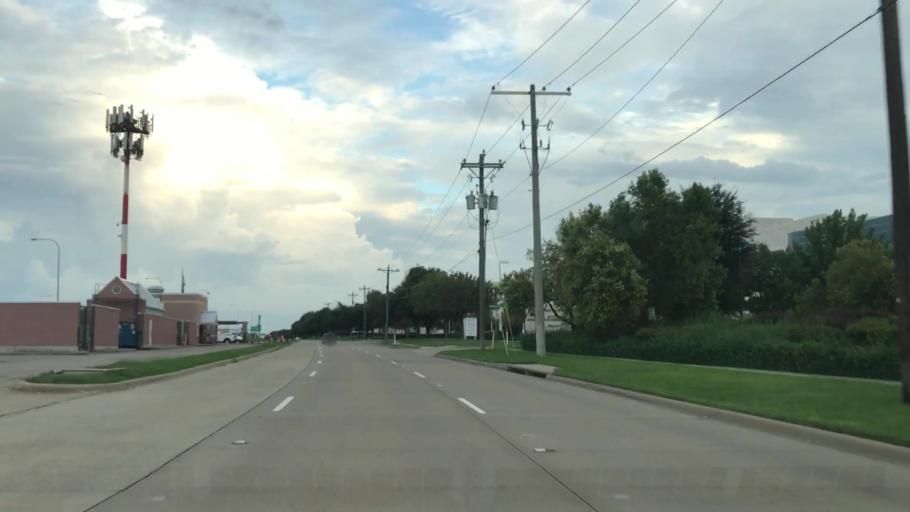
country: US
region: Texas
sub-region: Denton County
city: The Colony
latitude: 33.0414
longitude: -96.8302
